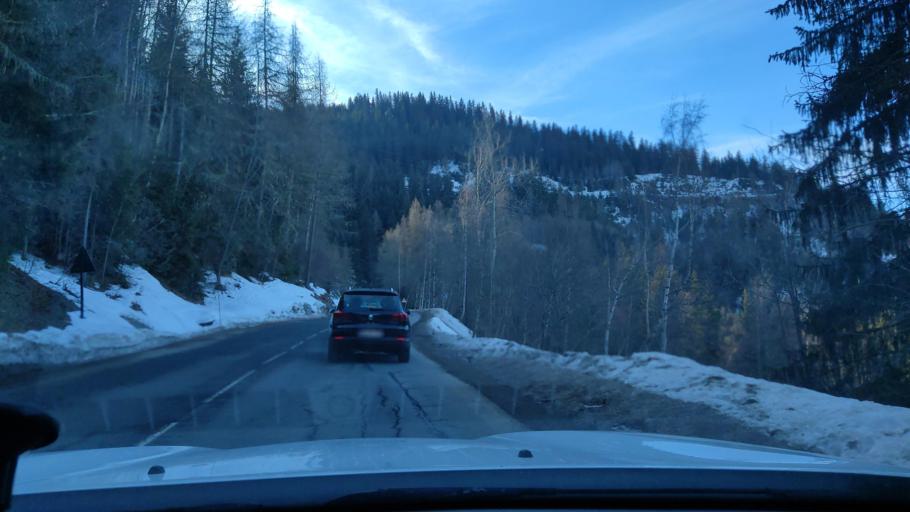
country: FR
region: Rhone-Alpes
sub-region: Departement de la Savoie
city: Bourg-Saint-Maurice
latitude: 45.5872
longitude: 6.7804
